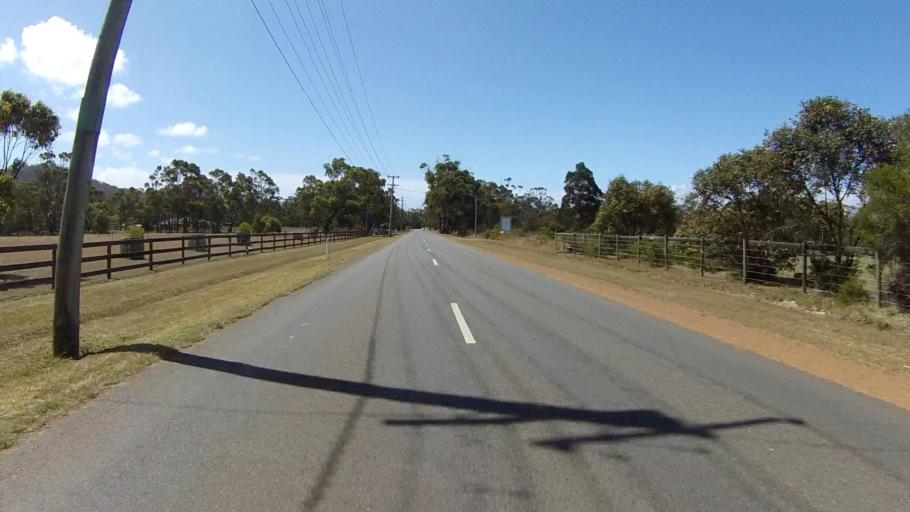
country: AU
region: Tasmania
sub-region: Clarence
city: Sandford
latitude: -42.9498
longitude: 147.4813
